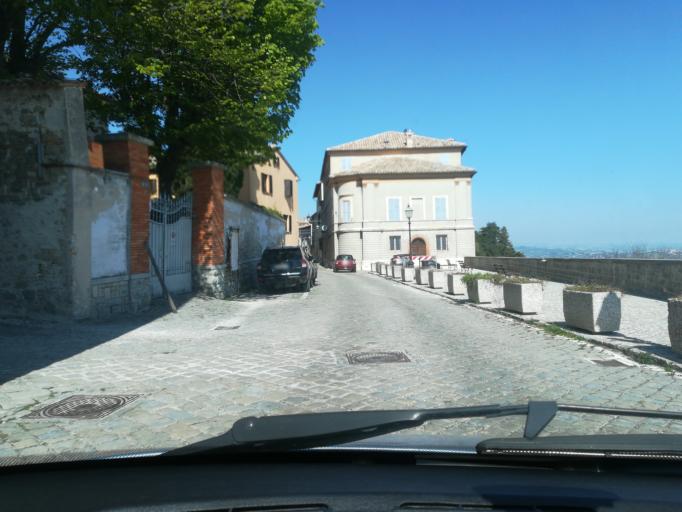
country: IT
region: The Marches
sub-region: Provincia di Macerata
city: Cingoli
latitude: 43.3762
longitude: 13.2166
